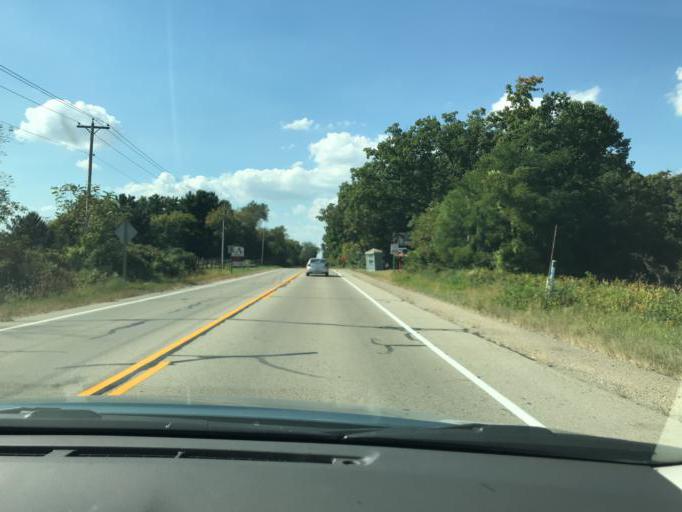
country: US
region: Wisconsin
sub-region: Walworth County
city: Williams Bay
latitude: 42.6028
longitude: -88.5465
